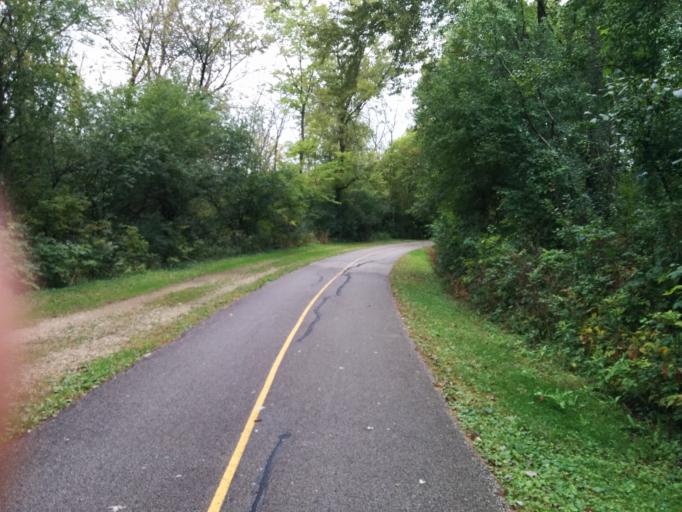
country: US
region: Illinois
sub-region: Cook County
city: Northfield
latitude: 42.1094
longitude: -87.7714
